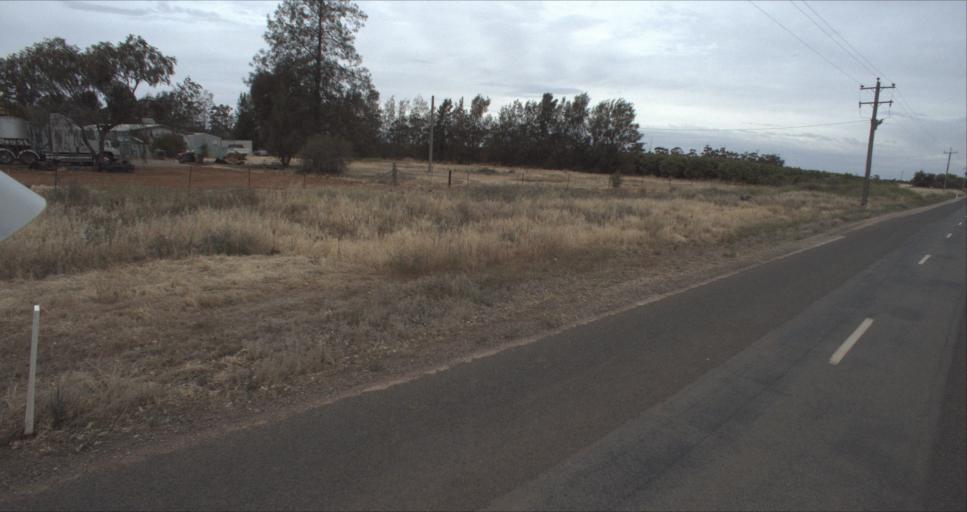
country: AU
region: New South Wales
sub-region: Leeton
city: Leeton
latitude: -34.4656
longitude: 146.3951
